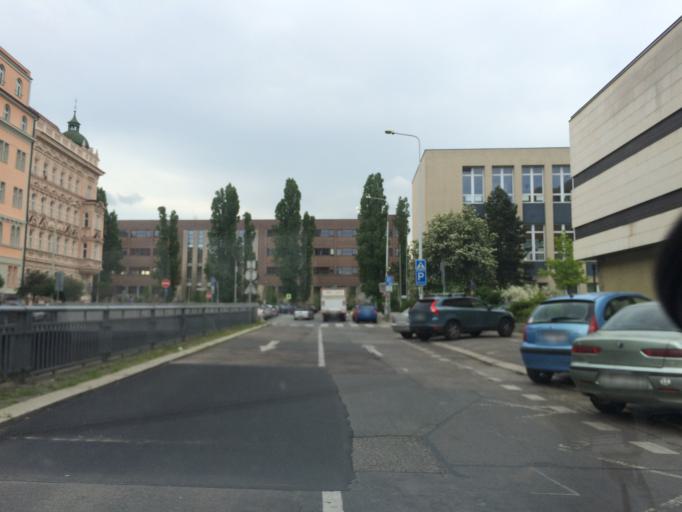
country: CZ
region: Praha
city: Prague
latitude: 50.0984
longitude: 14.4223
